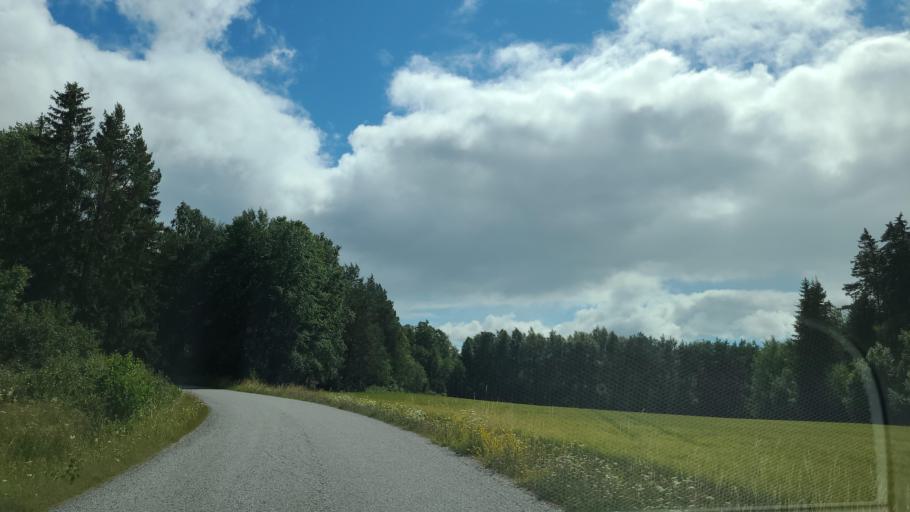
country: FI
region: Varsinais-Suomi
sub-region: Aboland-Turunmaa
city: Nagu
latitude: 60.1785
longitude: 22.0191
